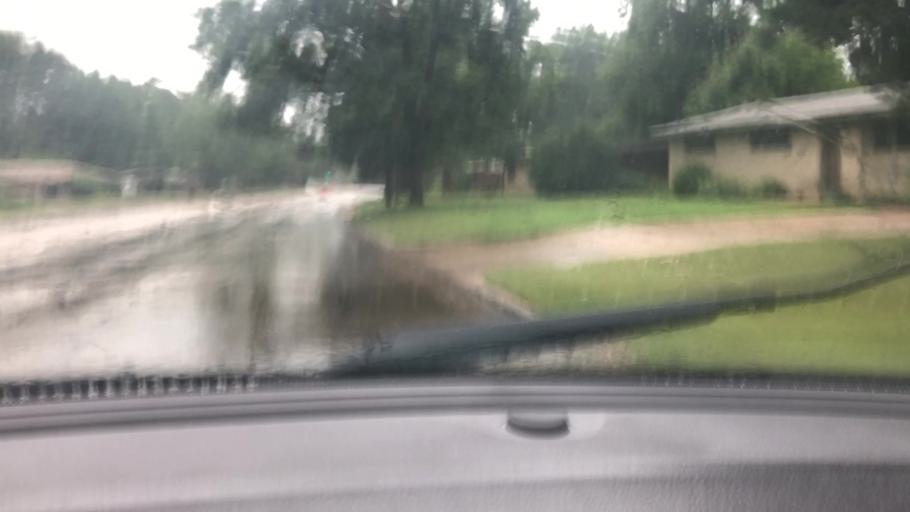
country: US
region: Texas
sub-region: Bowie County
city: Wake Village
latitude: 33.4496
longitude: -94.0802
